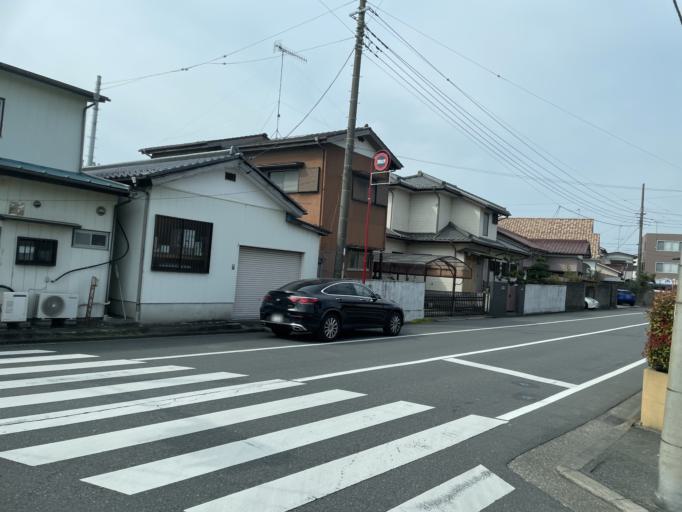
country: JP
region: Saitama
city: Gyoda
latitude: 36.1351
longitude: 139.4523
